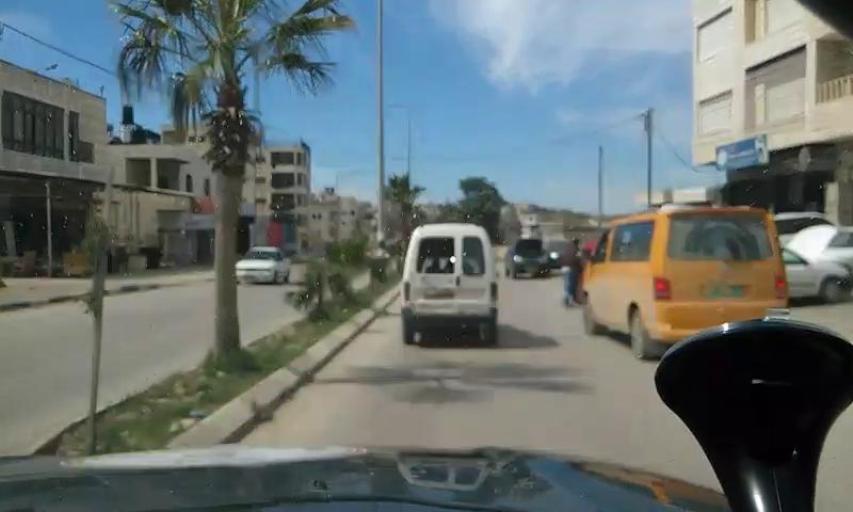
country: PS
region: West Bank
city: Al Judayrah
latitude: 31.8527
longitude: 35.1962
